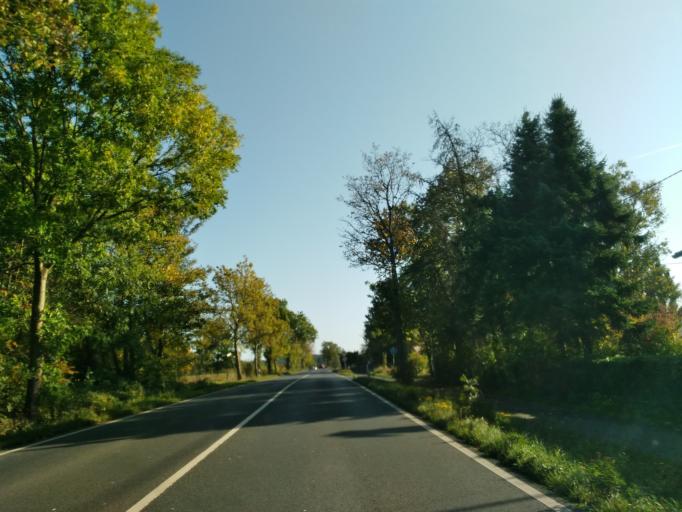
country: DE
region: Rheinland-Pfalz
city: Asbach
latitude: 50.7259
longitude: 7.3731
